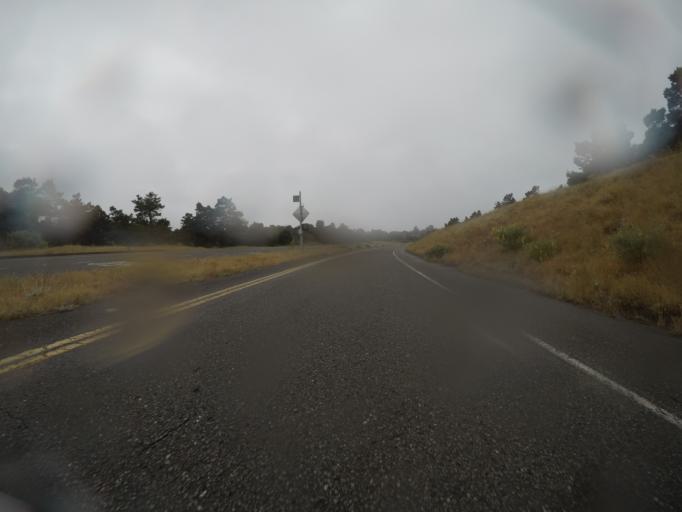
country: US
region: California
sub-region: Humboldt County
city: Eureka
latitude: 40.8244
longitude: -124.1782
